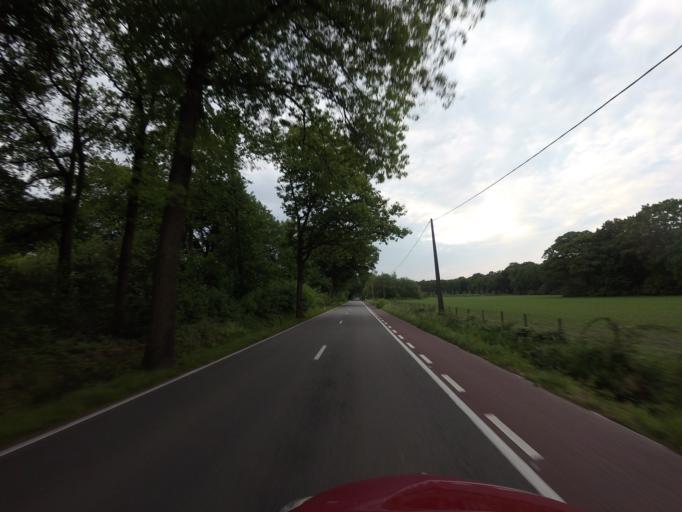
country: BE
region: Flanders
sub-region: Provincie Antwerpen
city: Oostmalle
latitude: 51.2833
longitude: 4.7583
